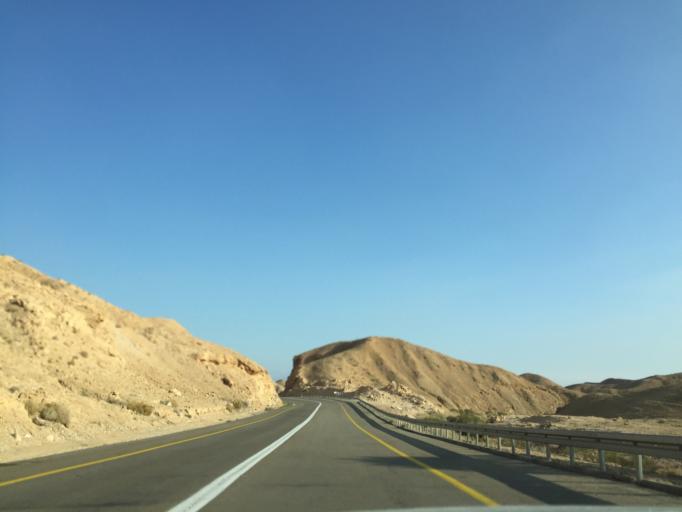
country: IL
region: Southern District
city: `En Boqeq
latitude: 31.1913
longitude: 35.2810
